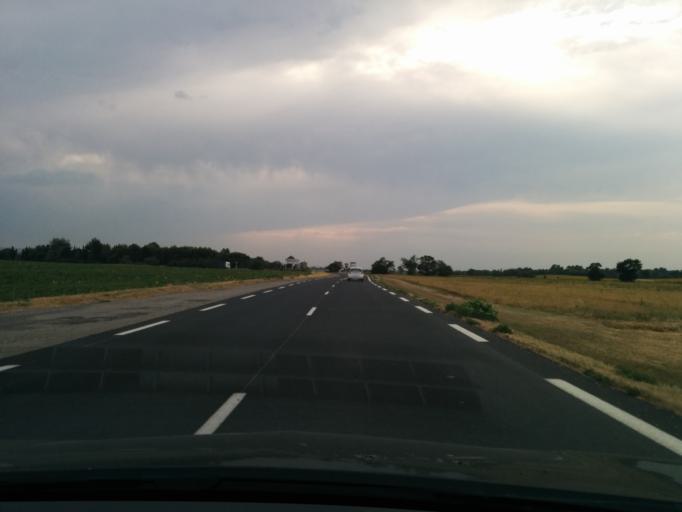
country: FR
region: Languedoc-Roussillon
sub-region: Departement de l'Aude
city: Bram
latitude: 43.2604
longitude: 2.1369
